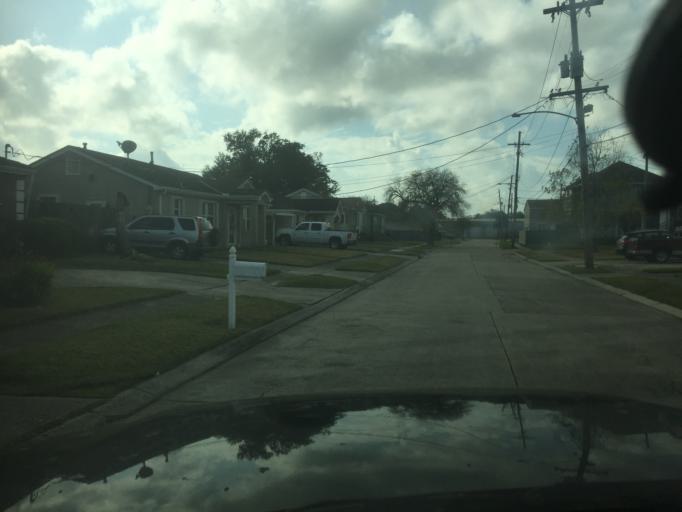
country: US
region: Louisiana
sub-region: Orleans Parish
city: New Orleans
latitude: 29.9906
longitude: -90.0788
